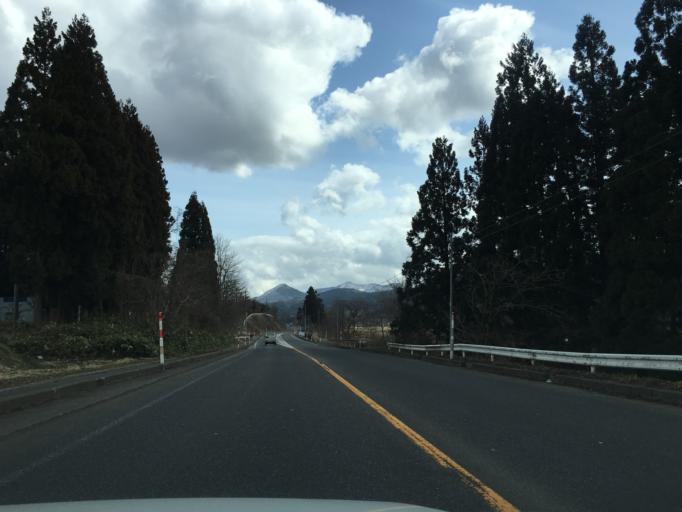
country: JP
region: Akita
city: Odate
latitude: 40.2235
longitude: 140.6044
